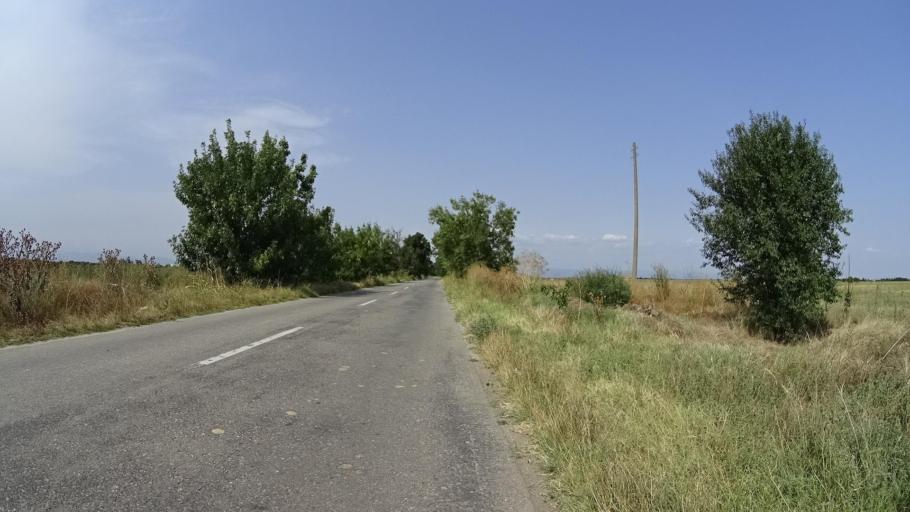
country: BG
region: Plovdiv
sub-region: Obshtina Plovdiv
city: Plovdiv
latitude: 42.2529
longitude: 24.7981
